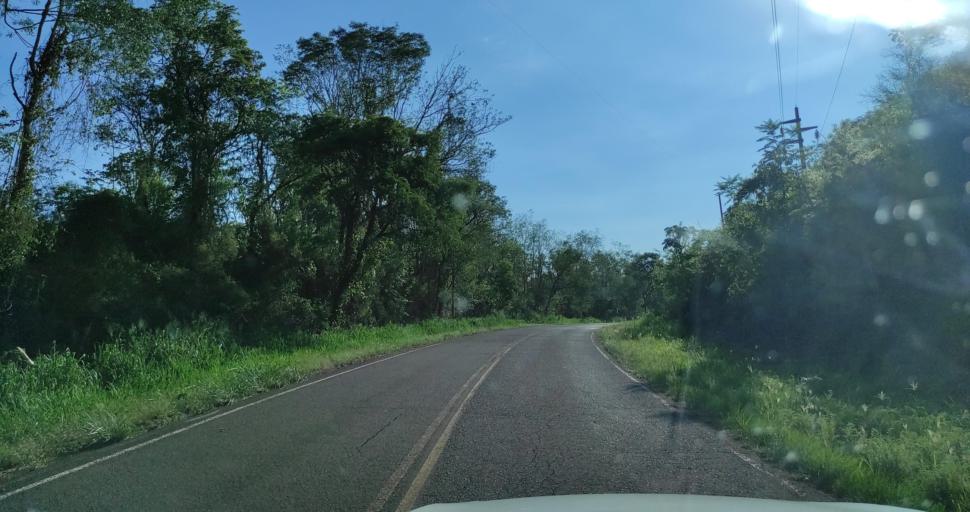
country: AR
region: Misiones
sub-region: Departamento de Eldorado
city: Eldorado
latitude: -26.3750
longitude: -54.3247
